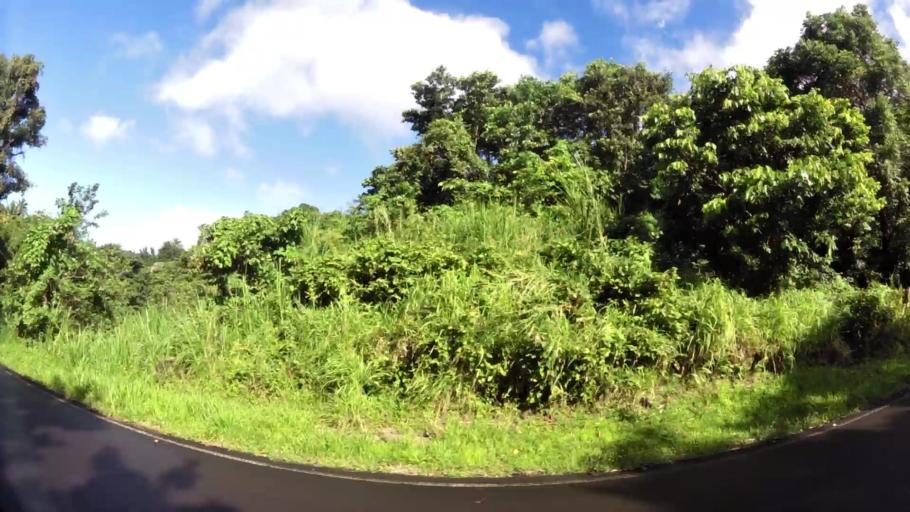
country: LC
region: Soufriere
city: Soufriere
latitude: 13.8682
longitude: -61.0462
